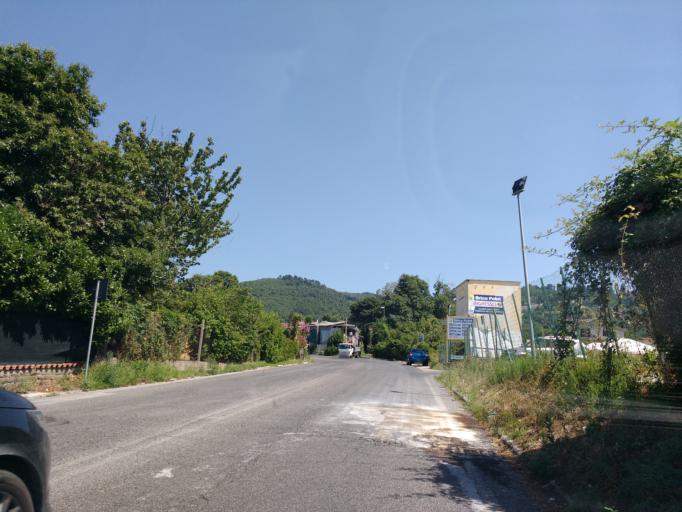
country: IT
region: Latium
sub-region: Citta metropolitana di Roma Capitale
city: Rocca di Papa
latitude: 41.7708
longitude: 12.7036
